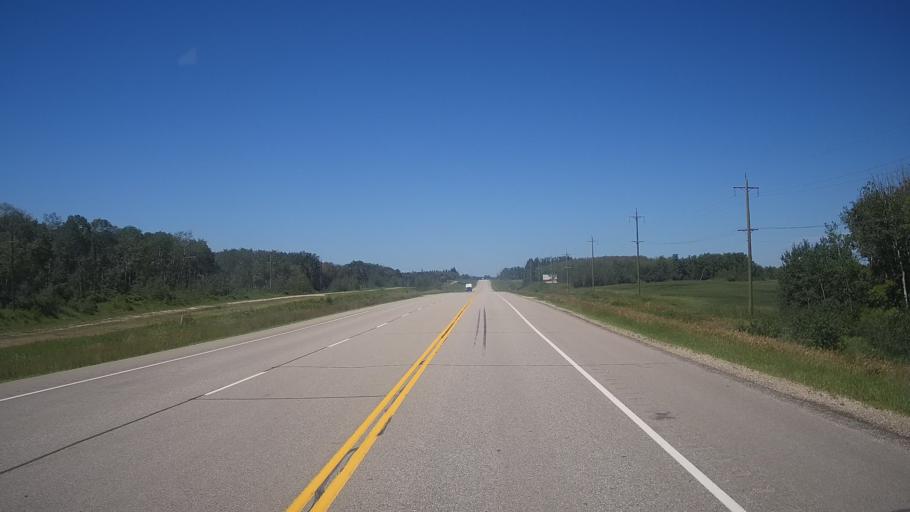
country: CA
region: Manitoba
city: Neepawa
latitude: 50.2253
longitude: -99.3502
